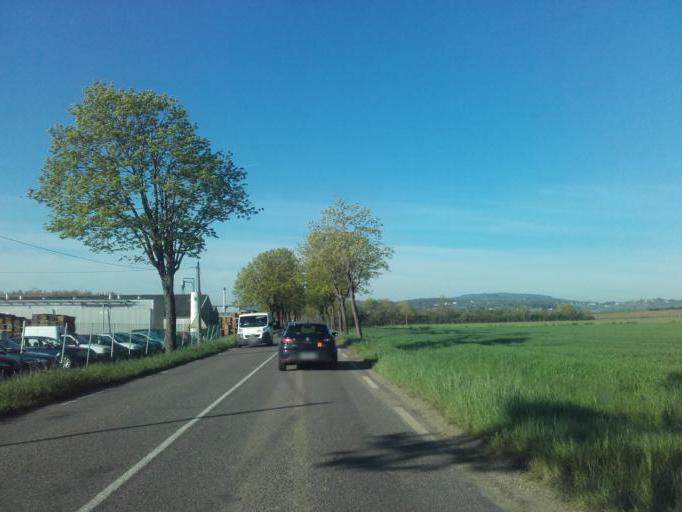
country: FR
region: Bourgogne
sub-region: Departement de Saone-et-Loire
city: Givry
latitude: 46.7632
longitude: 4.7365
